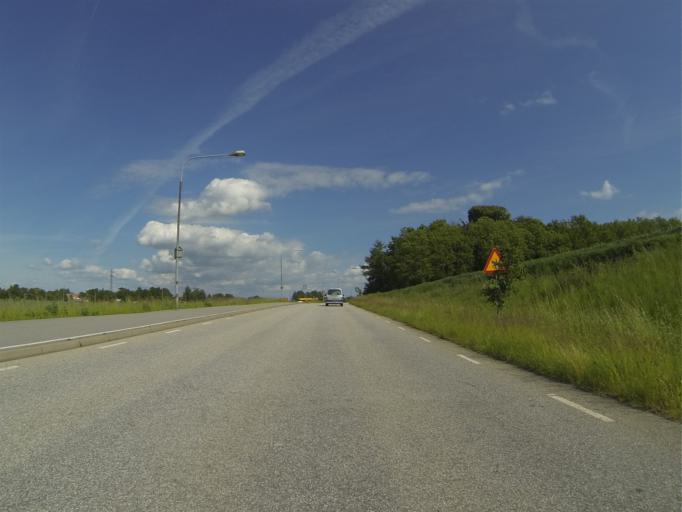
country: SE
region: Skane
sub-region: Burlovs Kommun
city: Arloev
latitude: 55.6340
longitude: 13.0932
